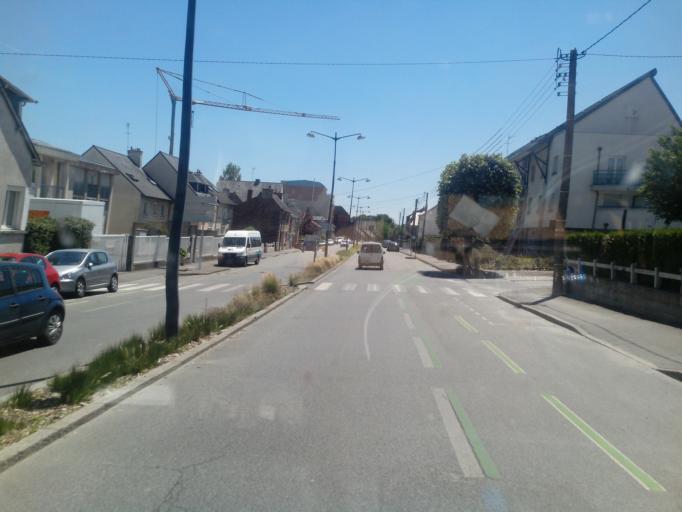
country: FR
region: Brittany
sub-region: Departement d'Ille-et-Vilaine
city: Rennes
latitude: 48.1186
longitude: -1.6497
